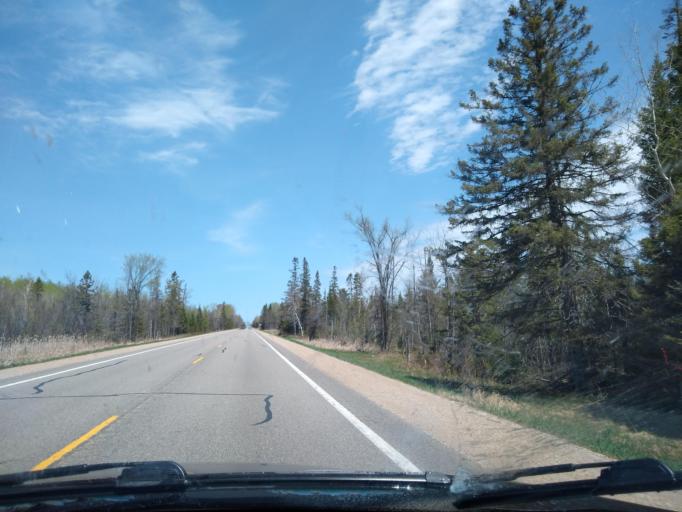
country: US
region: Michigan
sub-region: Delta County
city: Gladstone
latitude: 46.0586
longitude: -86.9812
